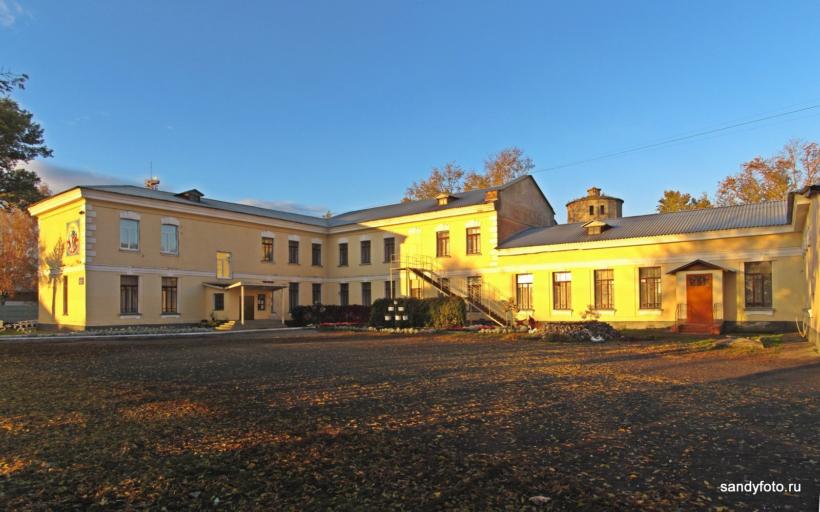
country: RU
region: Chelyabinsk
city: Troitsk
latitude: 54.1100
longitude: 61.5703
